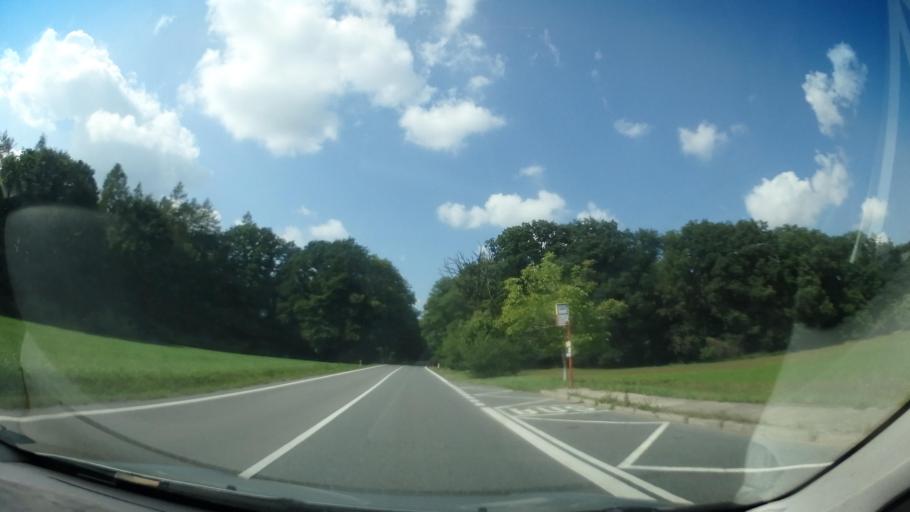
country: CZ
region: Central Bohemia
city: Kostelec nad Cernymi Lesy
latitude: 49.9837
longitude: 14.8769
